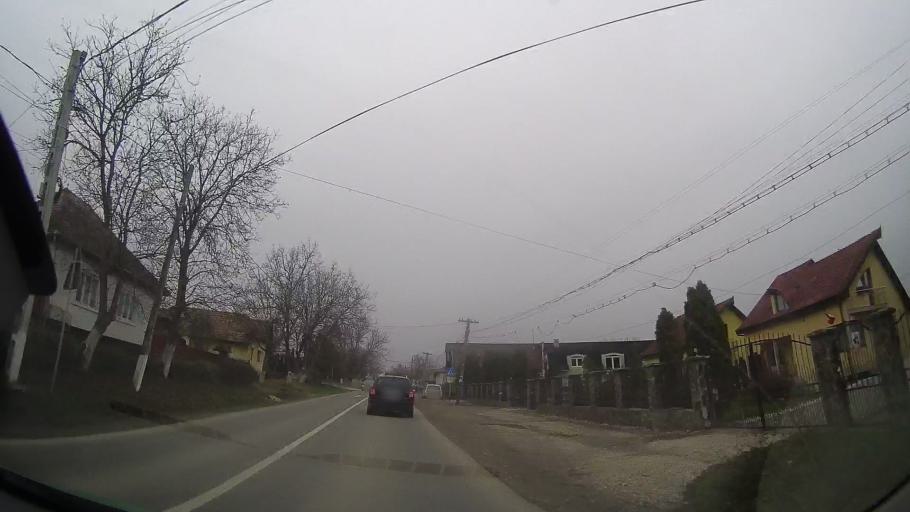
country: RO
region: Mures
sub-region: Comuna Ceausu de Campie
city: Ceausu de Campie
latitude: 46.6077
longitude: 24.5295
